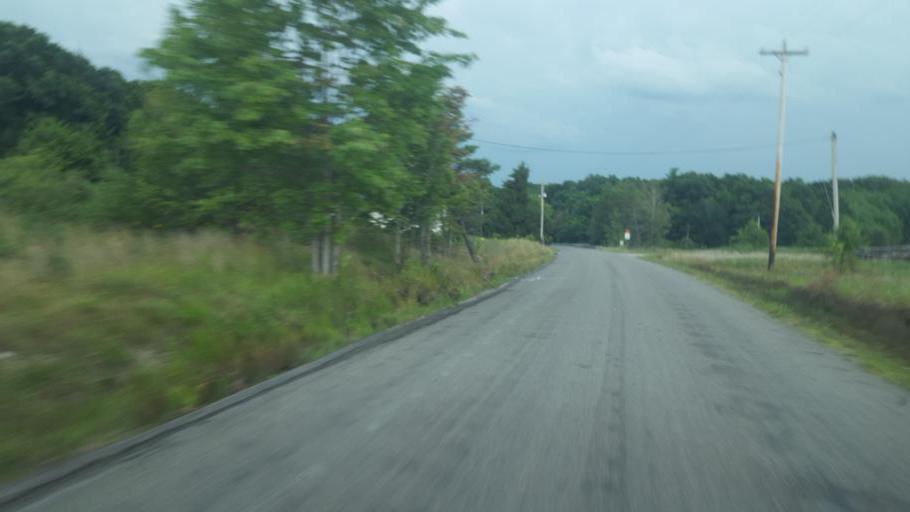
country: US
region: Pennsylvania
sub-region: Clarion County
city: Knox
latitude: 41.1800
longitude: -79.5405
